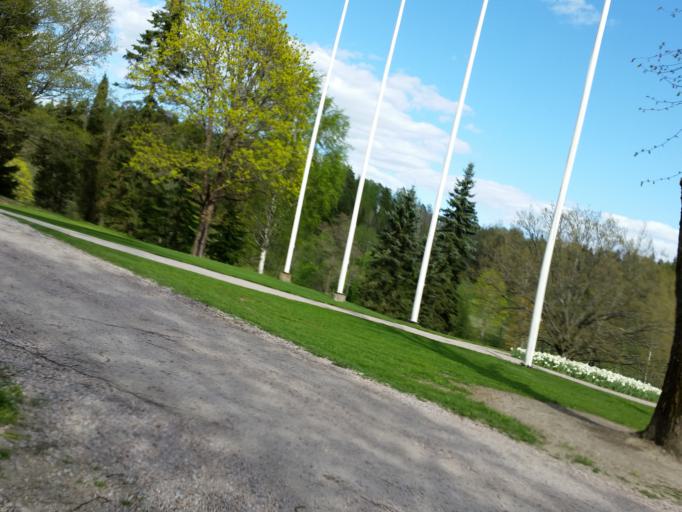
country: FI
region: Uusimaa
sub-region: Helsinki
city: Espoo
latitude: 60.2194
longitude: 24.6172
